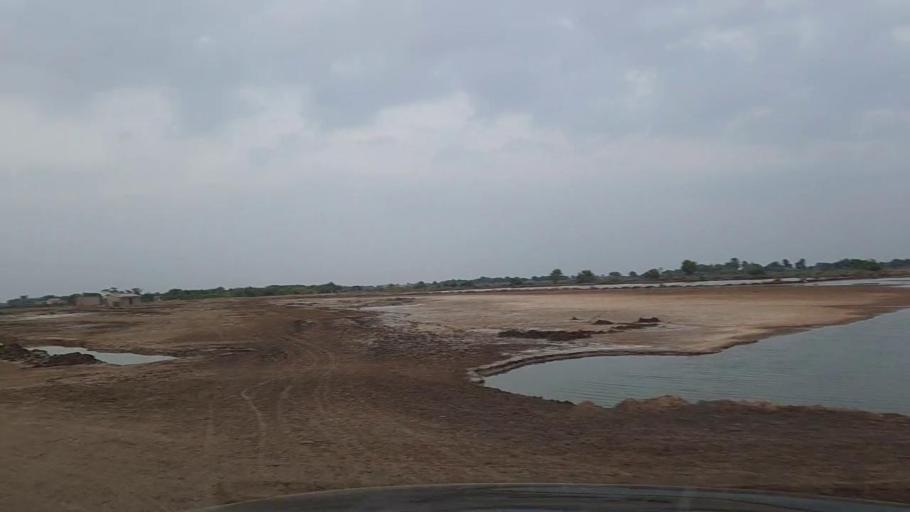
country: PK
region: Sindh
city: Jati
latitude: 24.4976
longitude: 68.3931
